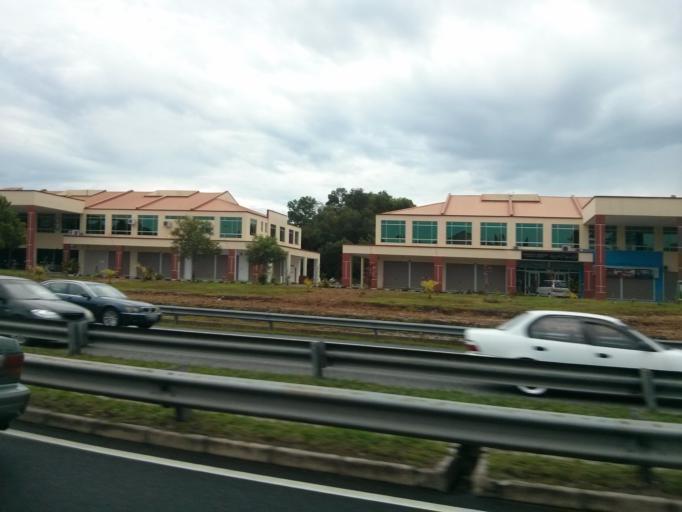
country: BN
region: Brunei and Muara
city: Bandar Seri Begawan
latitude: 4.9240
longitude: 114.9109
